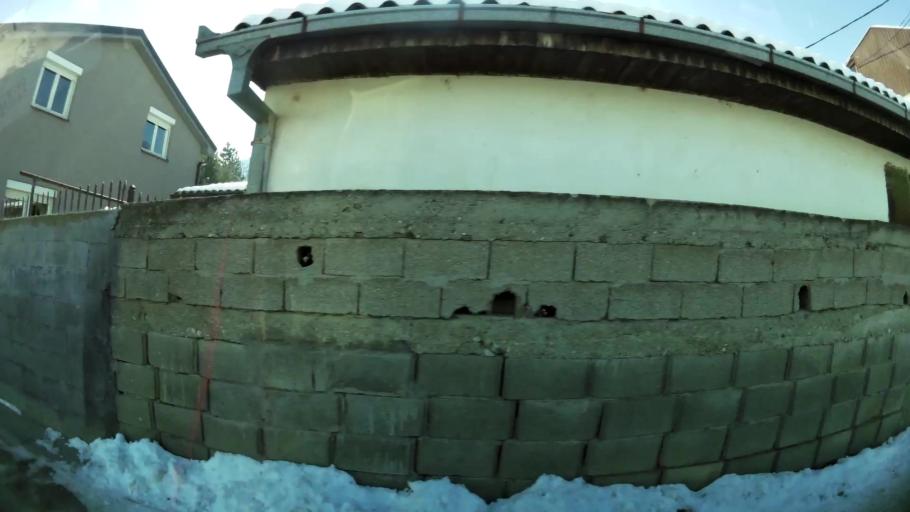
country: MK
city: Ljubin
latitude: 42.0017
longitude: 21.3162
